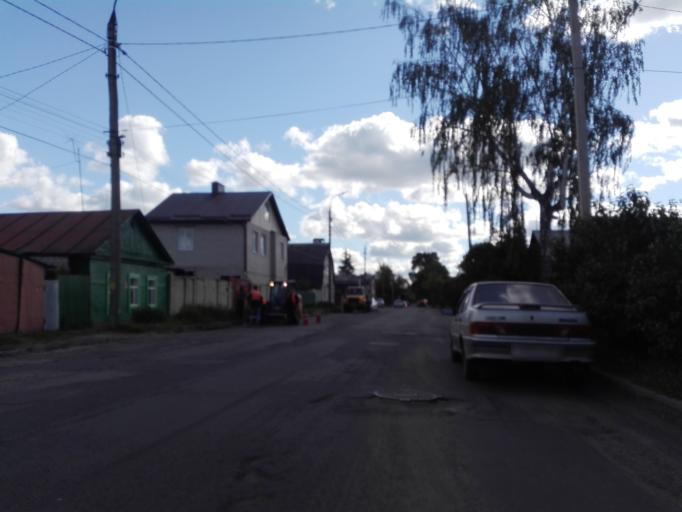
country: RU
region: Orjol
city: Orel
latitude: 52.9572
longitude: 36.0543
